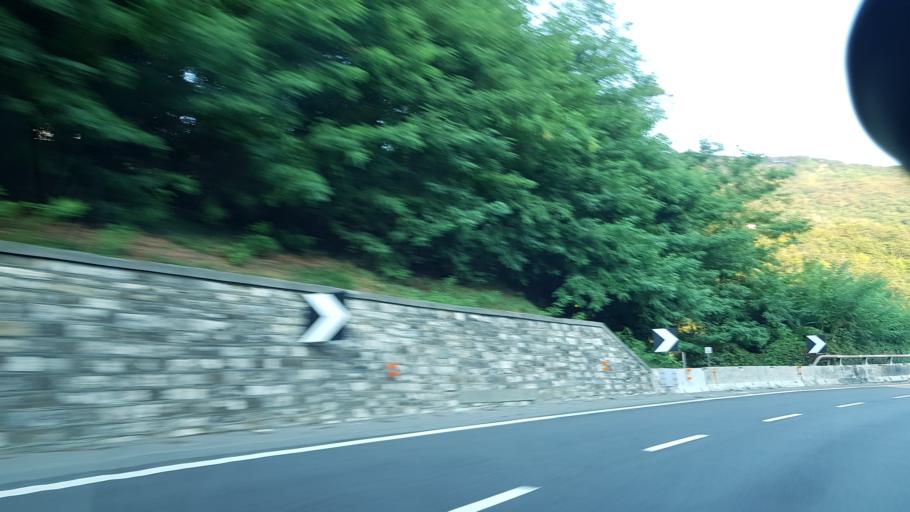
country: IT
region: Liguria
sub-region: Provincia di Genova
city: Busalla
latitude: 44.5413
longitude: 8.9456
